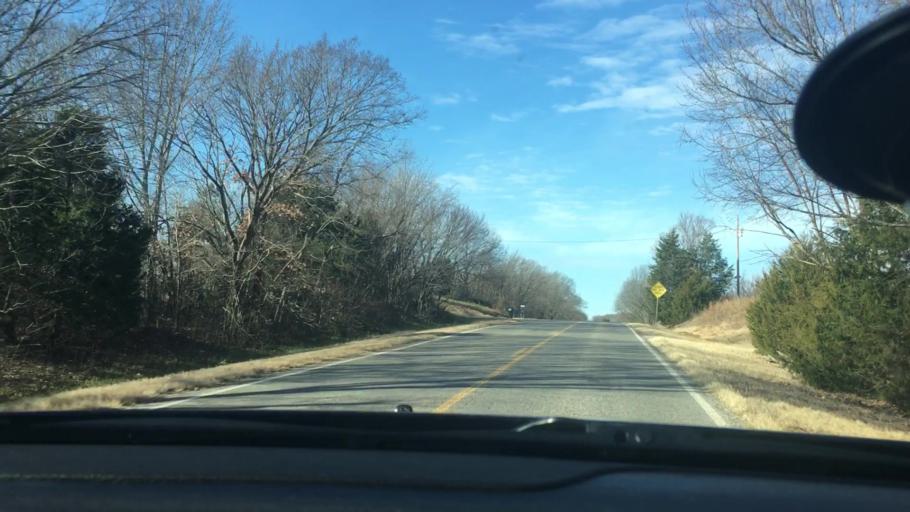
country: US
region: Oklahoma
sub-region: Seminole County
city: Konawa
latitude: 34.9856
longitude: -96.8226
